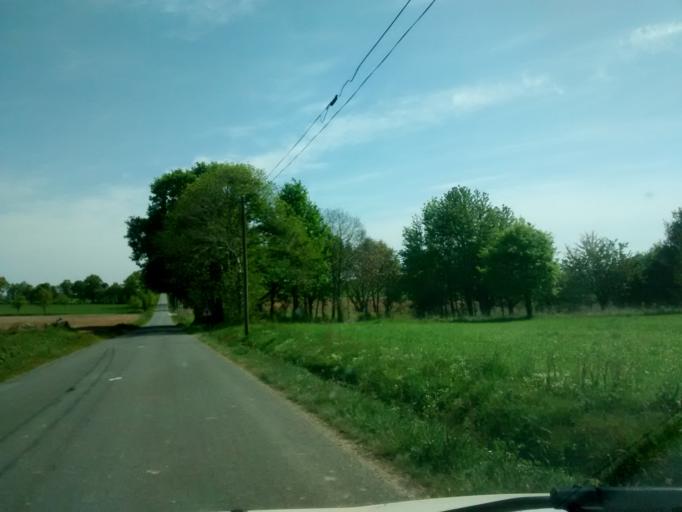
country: FR
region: Brittany
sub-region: Departement d'Ille-et-Vilaine
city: Messac
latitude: 47.7955
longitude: -1.7811
